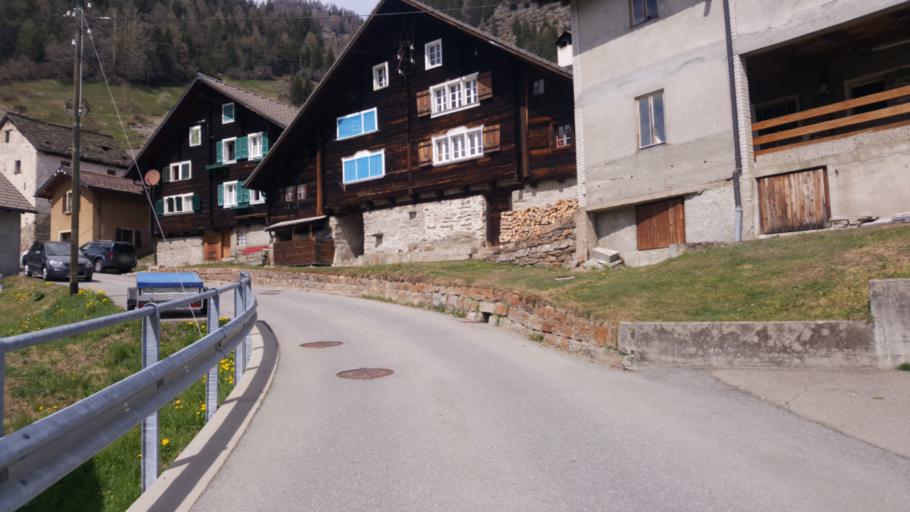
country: CH
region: Ticino
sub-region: Leventina District
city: Airolo
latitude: 46.5237
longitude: 8.6823
